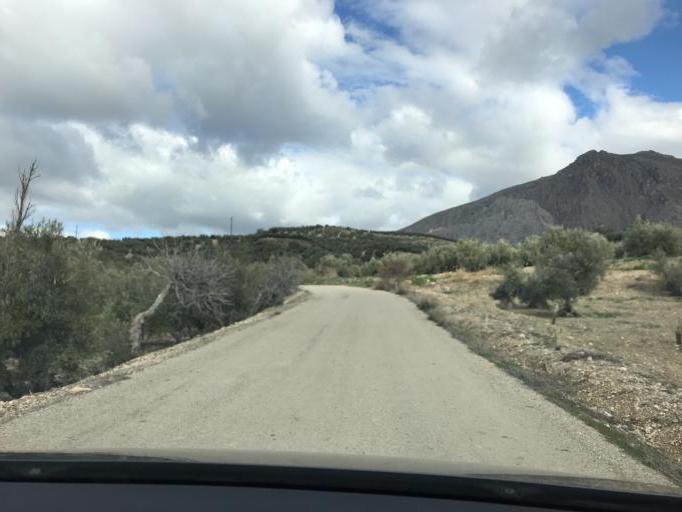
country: ES
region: Andalusia
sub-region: Provincia de Jaen
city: Jimena
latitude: 37.8129
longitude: -3.4249
